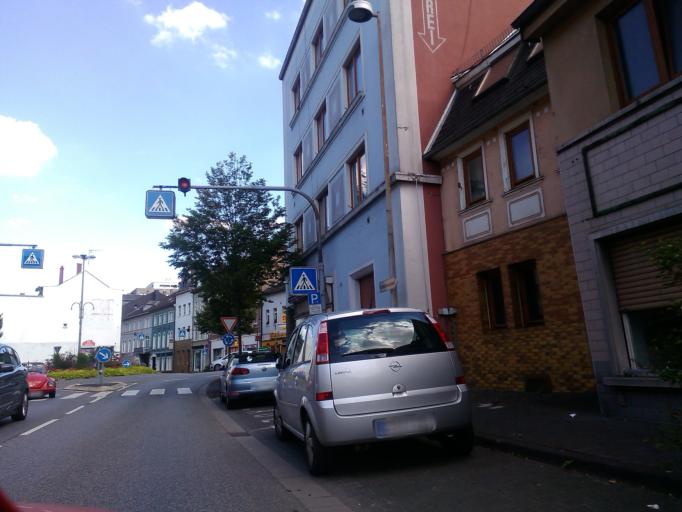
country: DE
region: Rheinland-Pfalz
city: Bingen am Rhein
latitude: 49.9689
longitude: 7.8966
